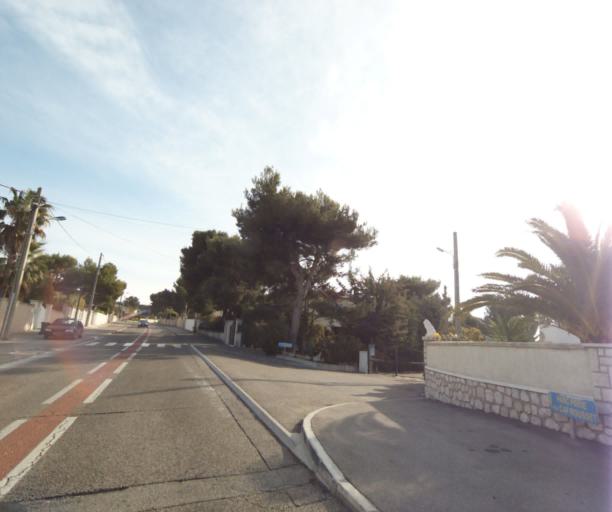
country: FR
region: Provence-Alpes-Cote d'Azur
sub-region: Departement des Bouches-du-Rhone
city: Carry-le-Rouet
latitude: 43.3320
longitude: 5.1615
